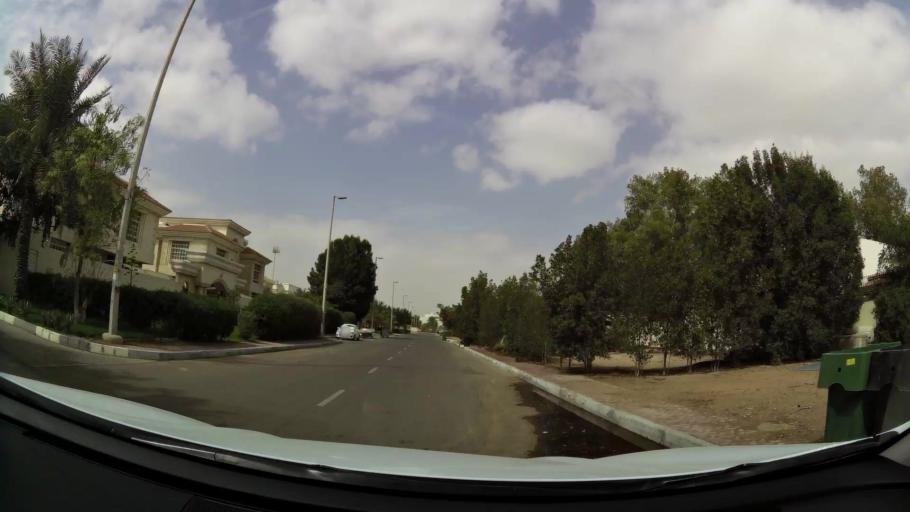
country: AE
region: Abu Dhabi
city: Abu Dhabi
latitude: 24.4038
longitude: 54.5179
